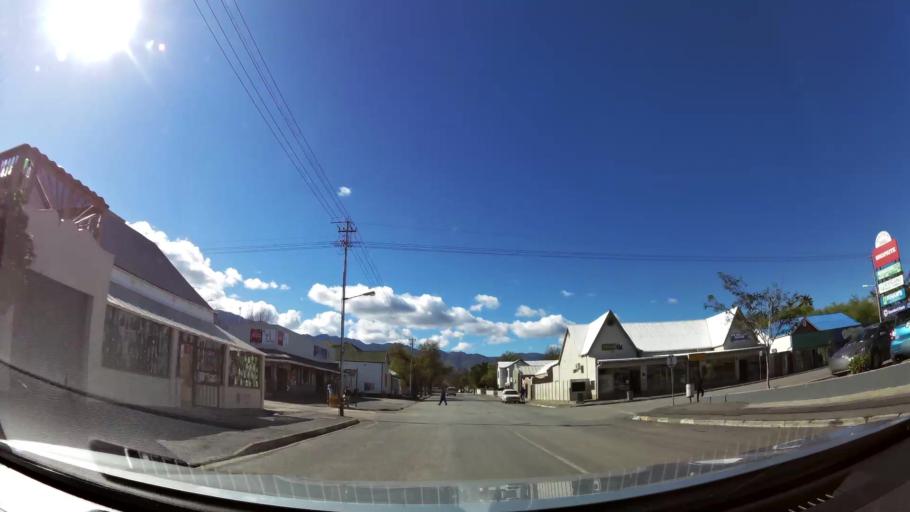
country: ZA
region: Western Cape
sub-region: Cape Winelands District Municipality
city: Ashton
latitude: -33.8015
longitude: 19.8806
